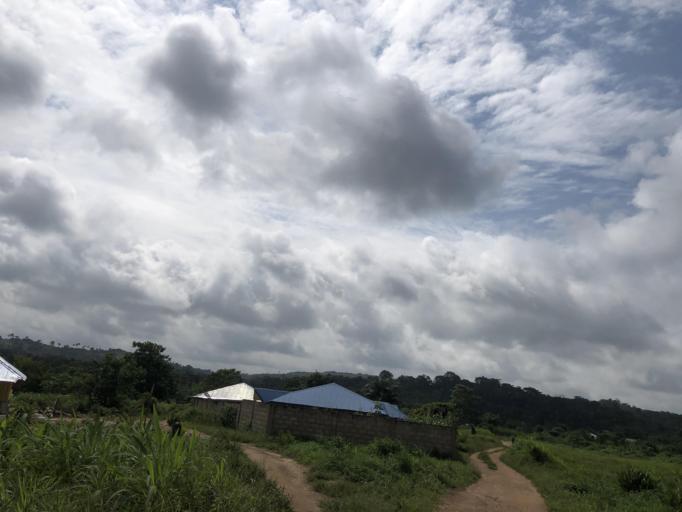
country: SL
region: Eastern Province
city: Kailahun
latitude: 8.2884
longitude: -10.5567
